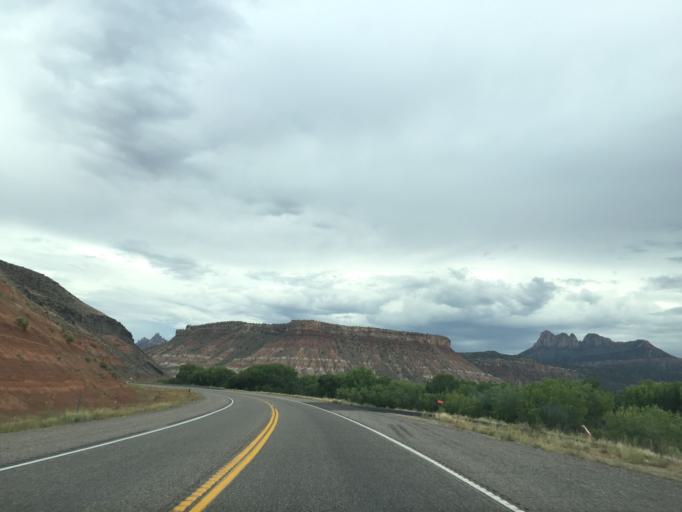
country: US
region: Utah
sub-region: Washington County
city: LaVerkin
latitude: 37.1737
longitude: -113.1136
